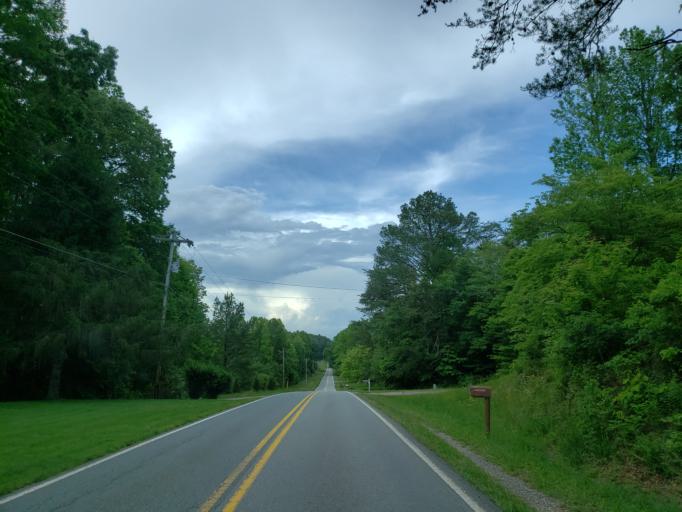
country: US
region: Georgia
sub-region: Fannin County
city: Blue Ridge
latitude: 34.8576
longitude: -84.3751
